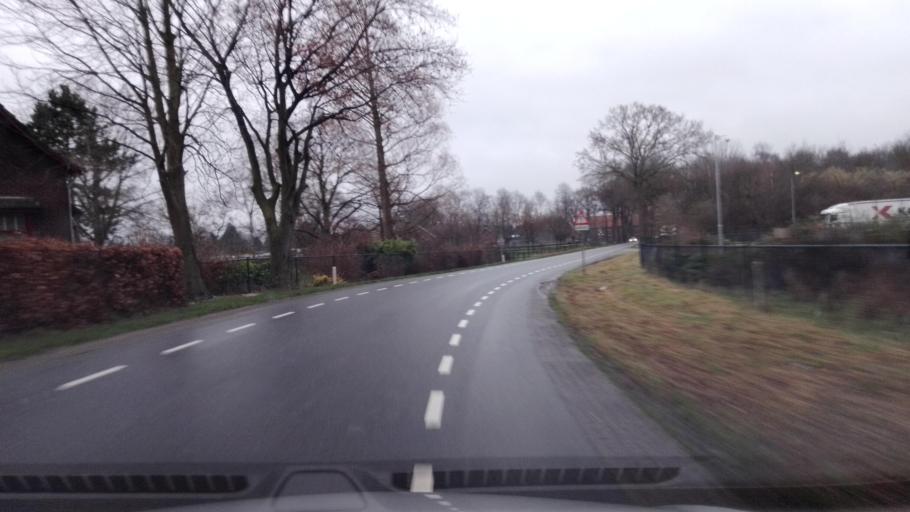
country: NL
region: Limburg
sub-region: Gemeente Bergen
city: Wellerlooi
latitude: 51.5080
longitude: 6.1516
